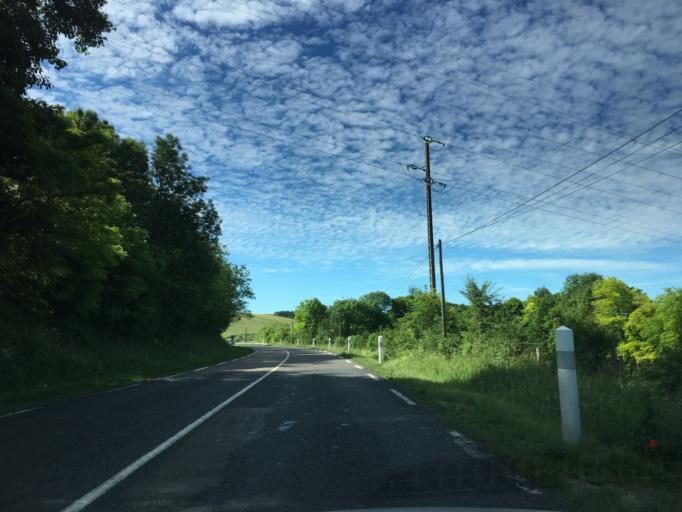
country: FR
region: Bourgogne
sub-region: Departement de l'Yonne
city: Auxerre
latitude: 47.7639
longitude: 3.5501
